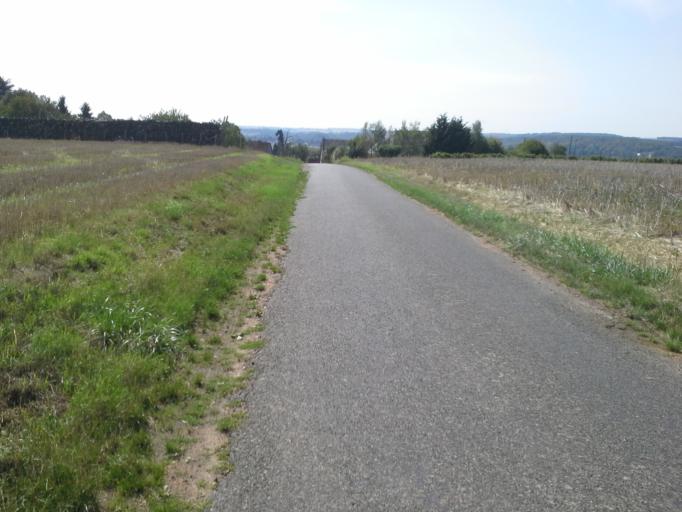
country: FR
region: Centre
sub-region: Departement du Loir-et-Cher
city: Villiers-sur-Loir
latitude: 47.8152
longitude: 0.9922
